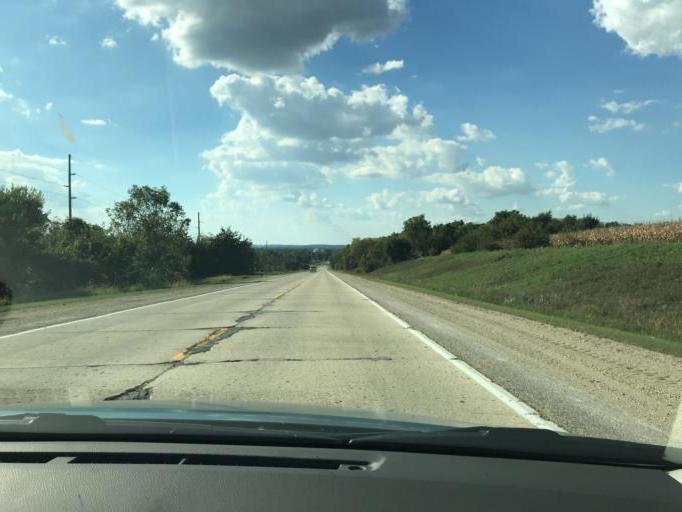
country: US
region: Wisconsin
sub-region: Green County
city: Brodhead
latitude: 42.5615
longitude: -89.3233
